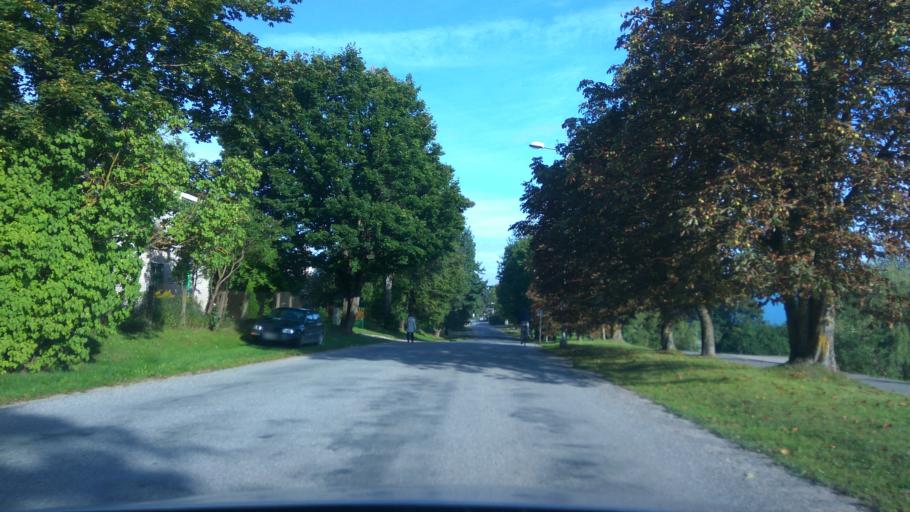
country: LV
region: Kuldigas Rajons
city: Kuldiga
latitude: 56.9753
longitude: 21.9636
